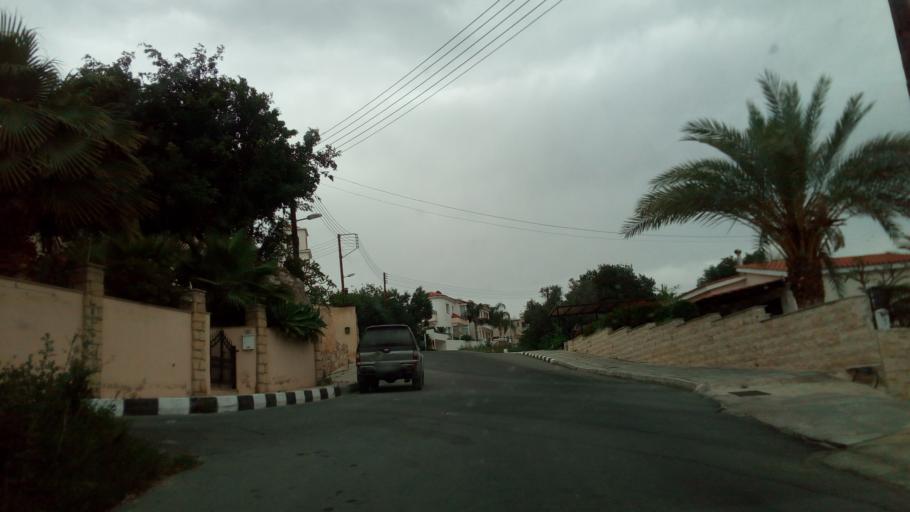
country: CY
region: Pafos
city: Mesogi
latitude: 34.8146
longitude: 32.4433
